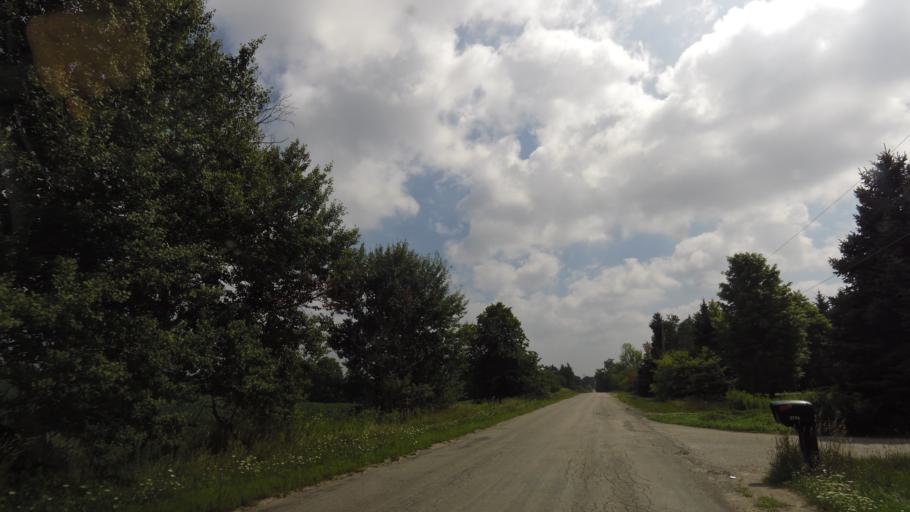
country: CA
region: Ontario
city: Oshawa
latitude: 44.0019
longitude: -78.8768
